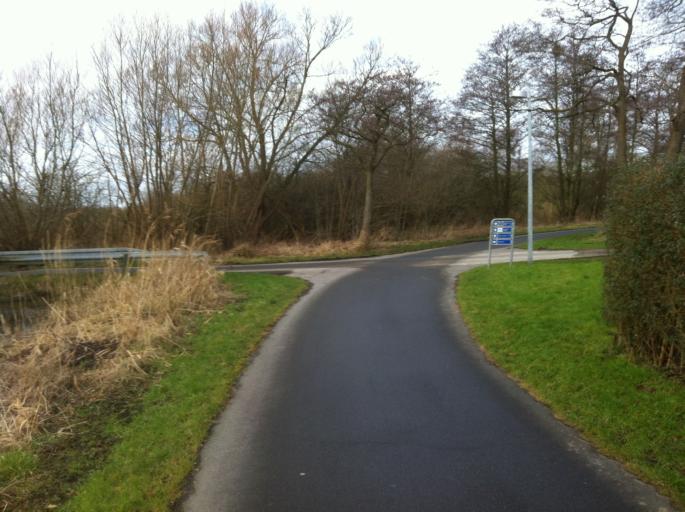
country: DK
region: South Denmark
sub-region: Odense Kommune
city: Odense
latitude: 55.4316
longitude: 10.3479
